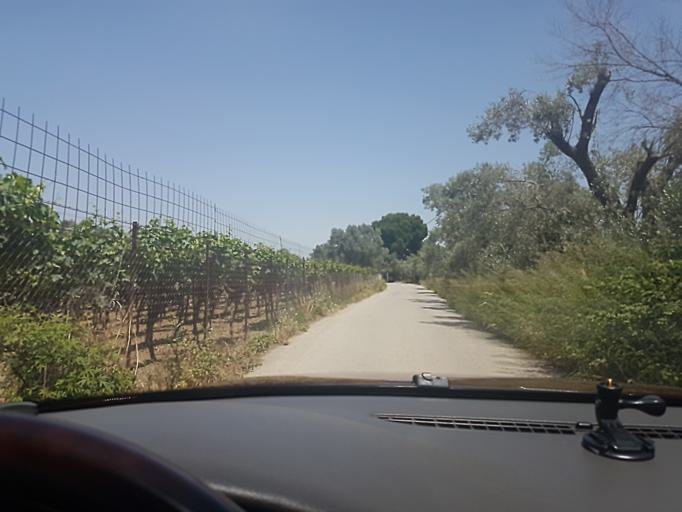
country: GR
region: Central Greece
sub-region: Nomos Evvoias
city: Vasilikon
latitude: 38.4099
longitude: 23.6660
